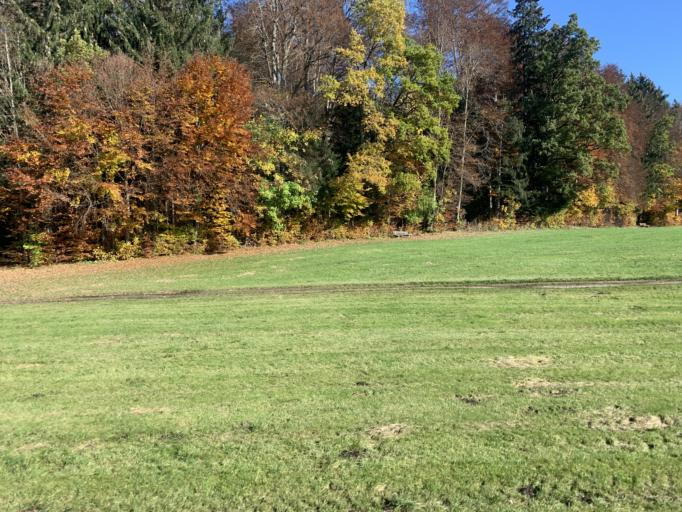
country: DE
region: Bavaria
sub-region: Upper Bavaria
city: Waakirchen
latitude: 47.7949
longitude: 11.6923
